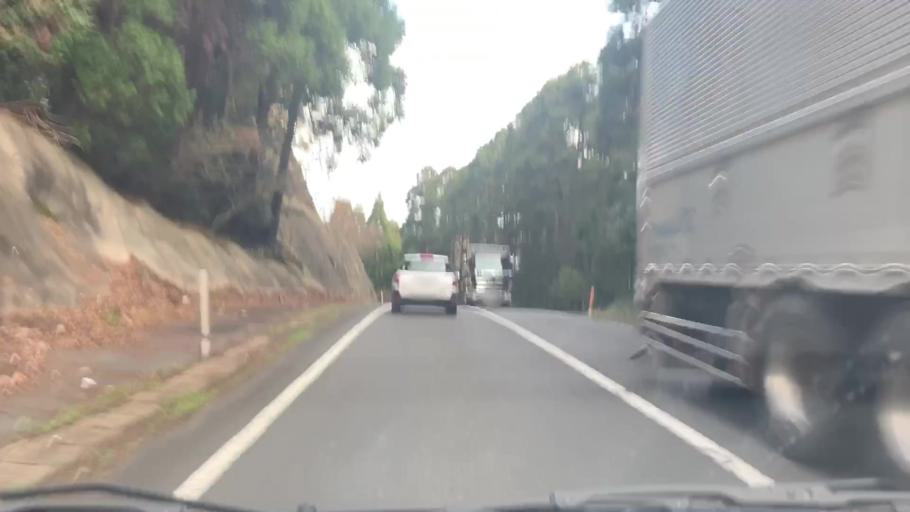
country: JP
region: Saga Prefecture
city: Imaricho-ko
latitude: 33.3296
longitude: 129.9703
